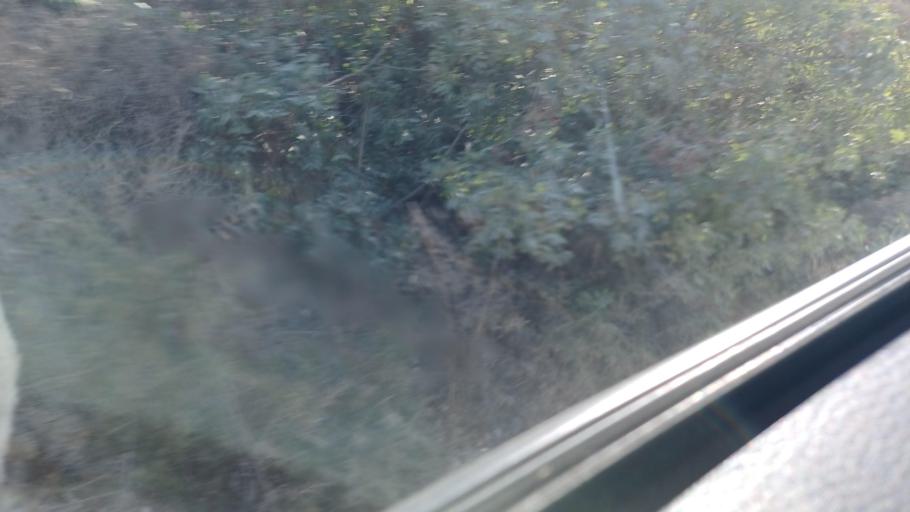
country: CY
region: Pafos
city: Tala
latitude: 34.8620
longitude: 32.4447
